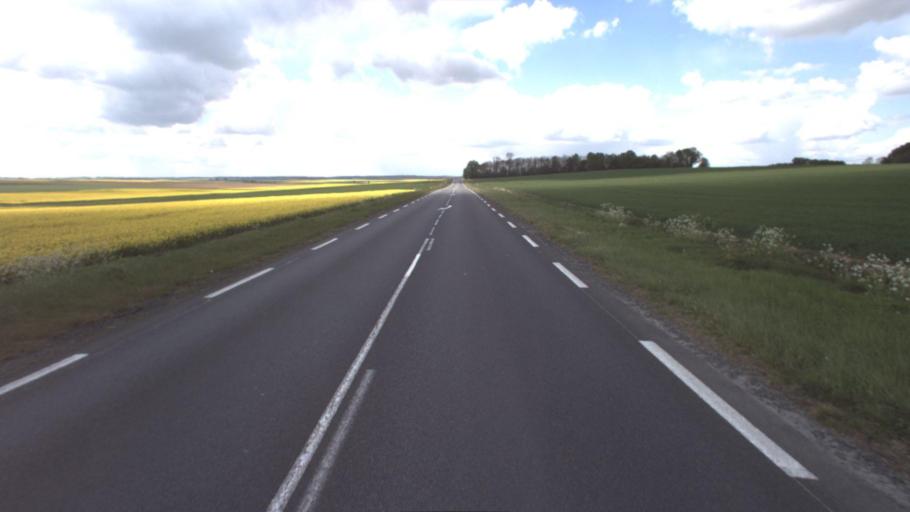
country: FR
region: Ile-de-France
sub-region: Departement de Seine-et-Marne
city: Villiers-Saint-Georges
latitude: 48.6922
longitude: 3.4202
